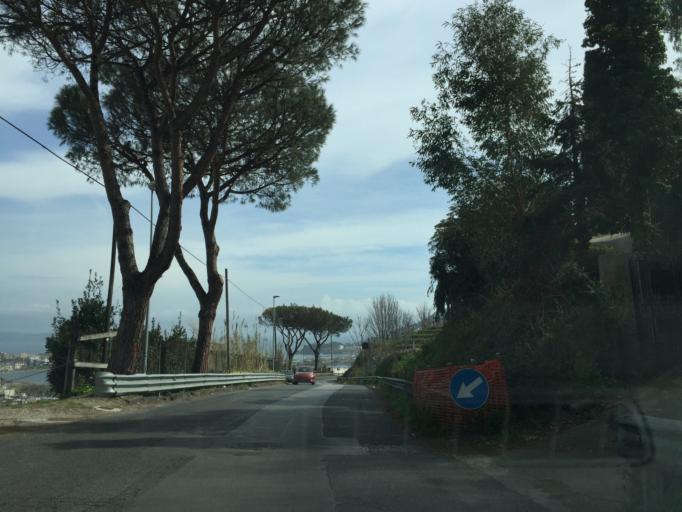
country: IT
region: Campania
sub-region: Provincia di Napoli
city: Monte di Procida
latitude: 40.7951
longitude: 14.0611
